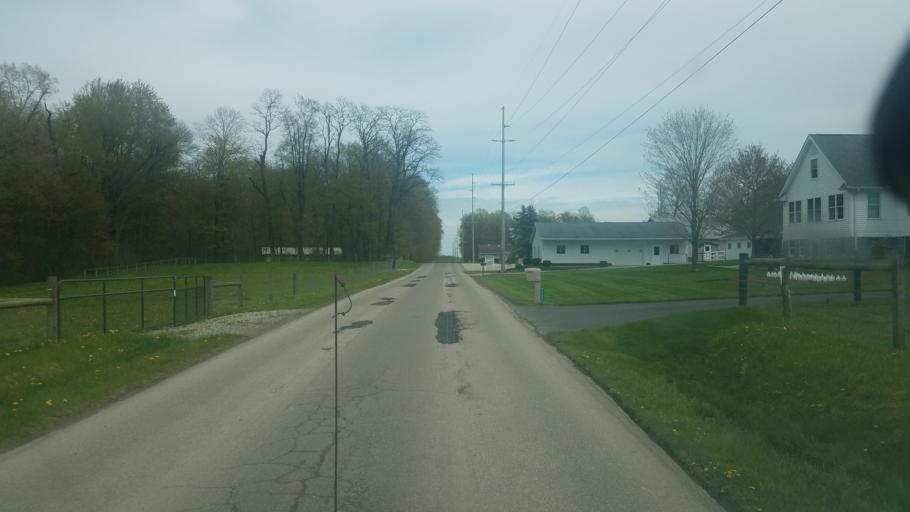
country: US
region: Ohio
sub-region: Wayne County
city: Apple Creek
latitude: 40.7120
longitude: -81.8097
